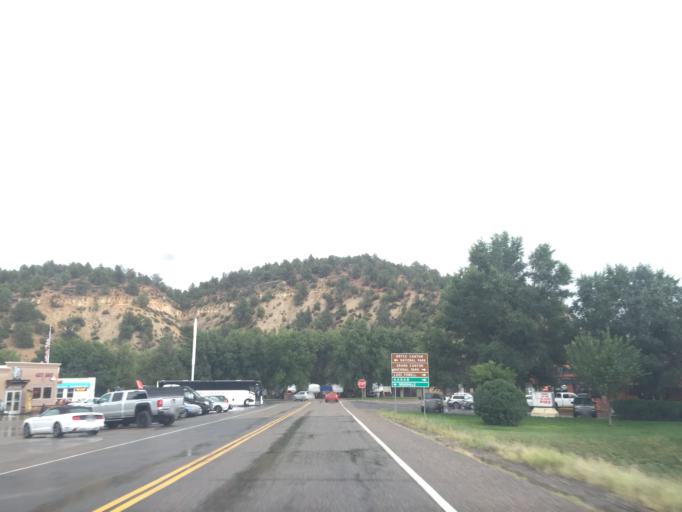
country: US
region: Utah
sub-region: Kane County
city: Kanab
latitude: 37.2239
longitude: -112.6820
